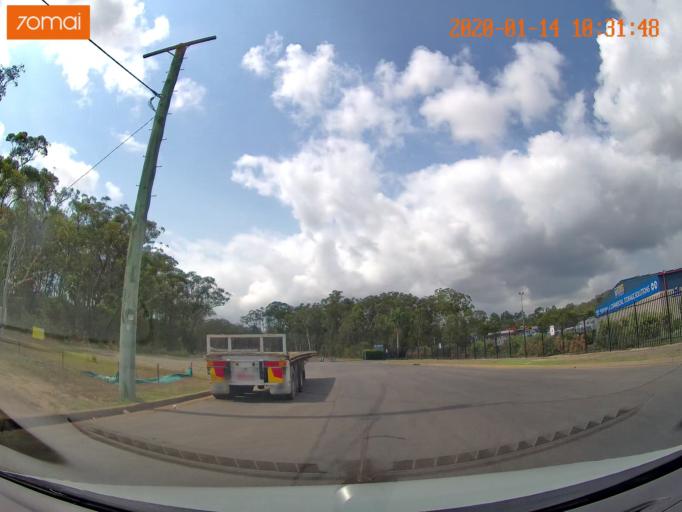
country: AU
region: New South Wales
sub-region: Lake Macquarie Shire
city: Dora Creek
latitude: -33.1208
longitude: 151.4709
